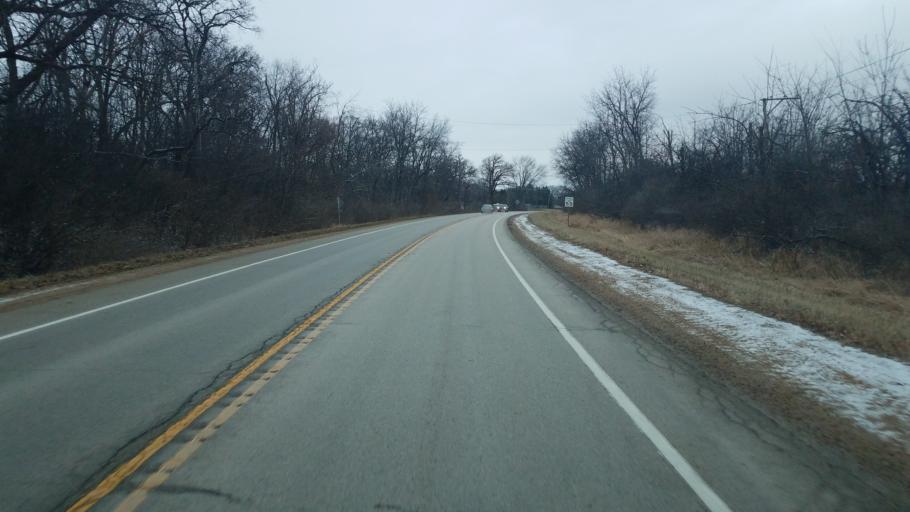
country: US
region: Illinois
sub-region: Kane County
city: Elburn
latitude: 41.8249
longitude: -88.4678
